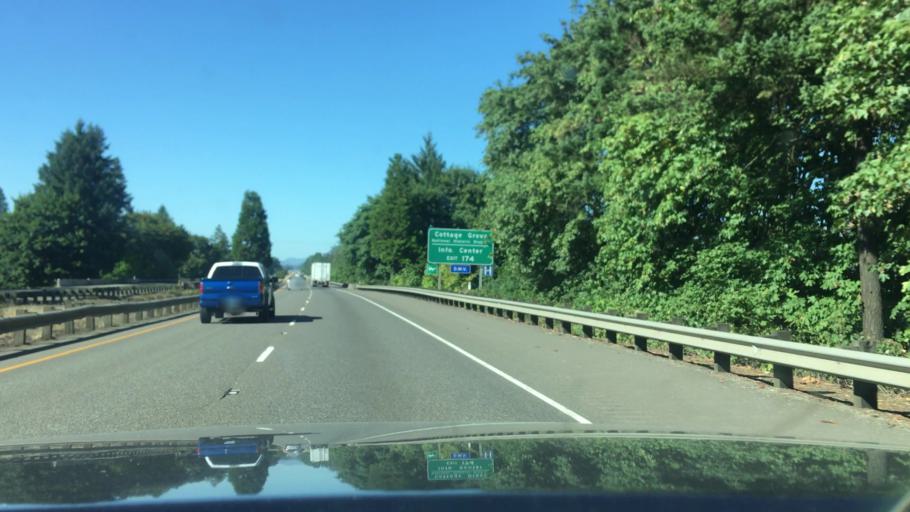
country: US
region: Oregon
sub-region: Lane County
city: Cottage Grove
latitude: 43.7986
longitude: -123.0456
